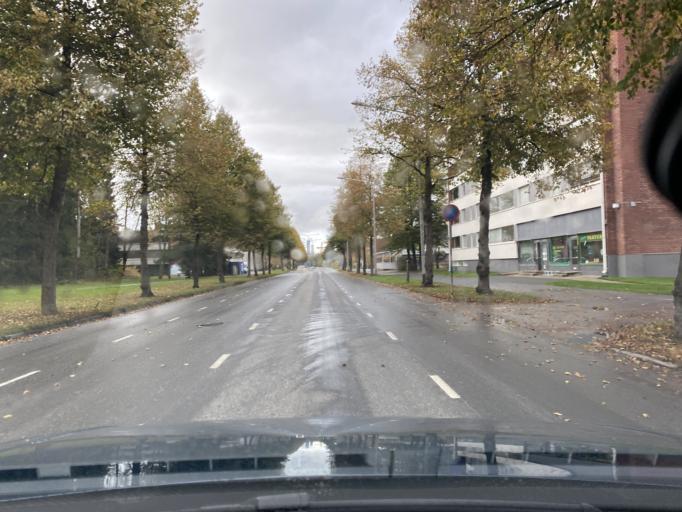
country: FI
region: Haeme
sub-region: Forssa
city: Forssa
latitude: 60.8187
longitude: 23.6103
